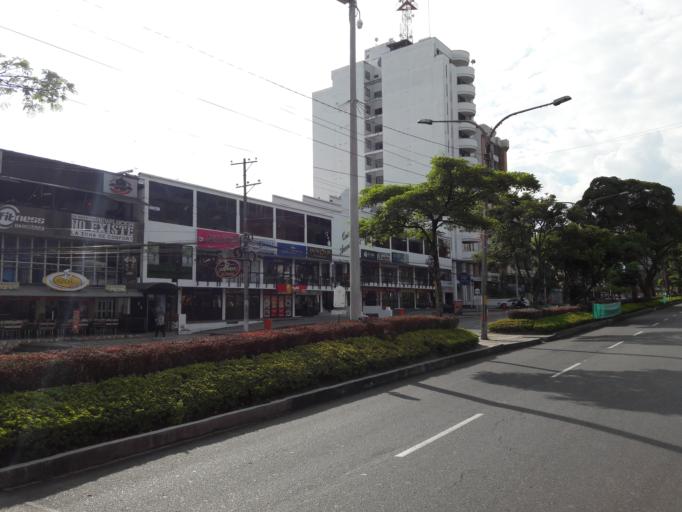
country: CO
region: Tolima
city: Ibague
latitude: 4.4372
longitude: -75.2152
